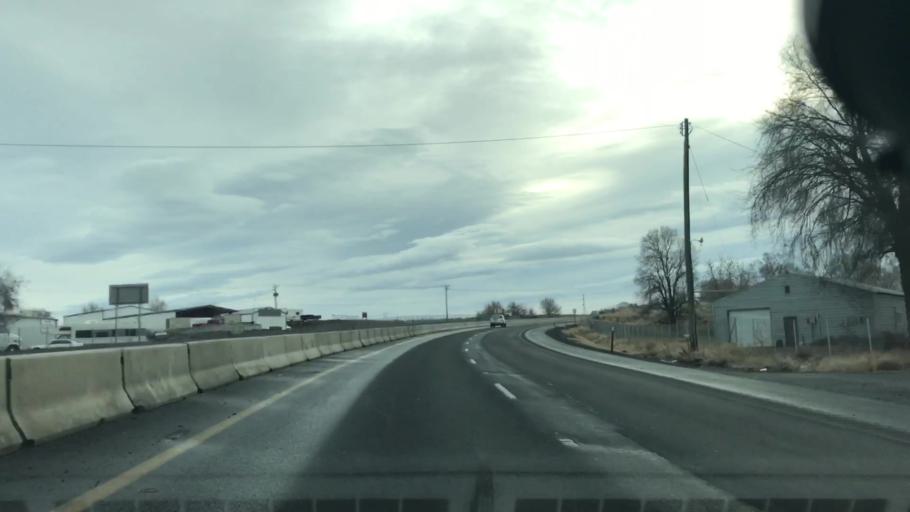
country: US
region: Washington
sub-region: Grant County
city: Moses Lake
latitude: 47.1383
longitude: -119.2593
